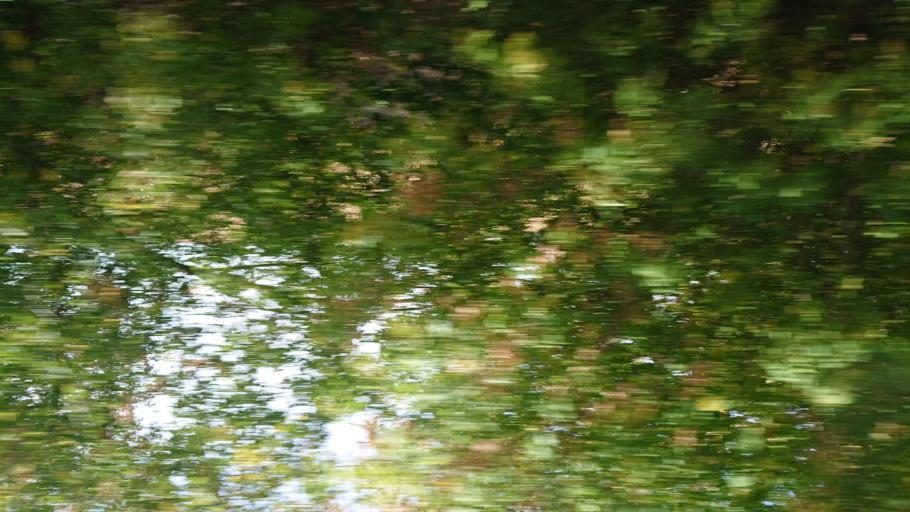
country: DE
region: Berlin
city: Buch
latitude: 52.6328
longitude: 13.5464
